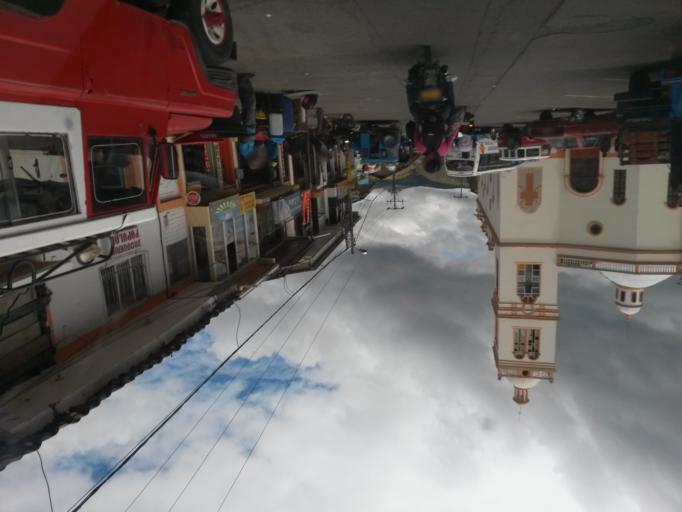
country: CO
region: Cauca
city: Silvia
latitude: 2.6108
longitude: -76.3790
